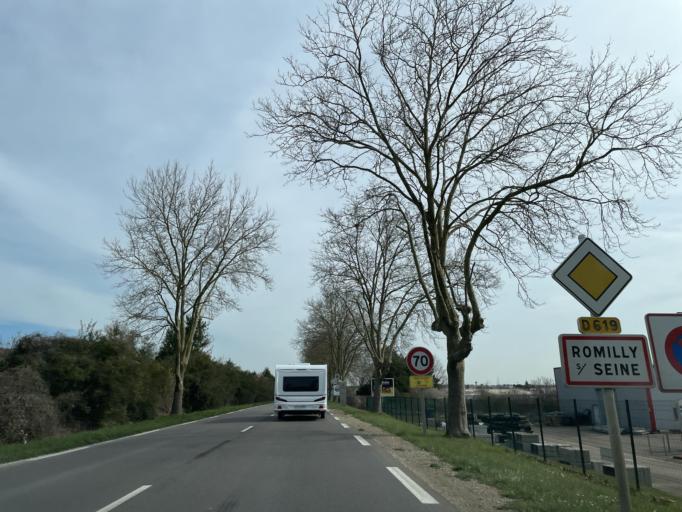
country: FR
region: Champagne-Ardenne
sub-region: Departement de l'Aube
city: Romilly-sur-Seine
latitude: 48.5091
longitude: 3.7081
